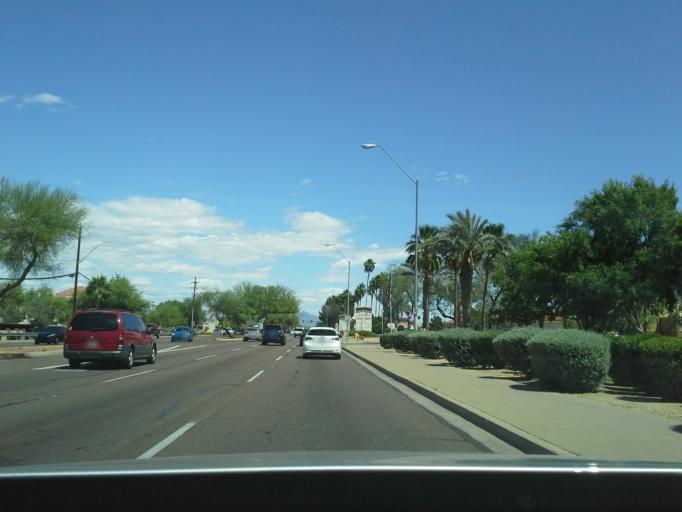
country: US
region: Arizona
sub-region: Maricopa County
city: Glendale
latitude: 33.6402
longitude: -112.0736
